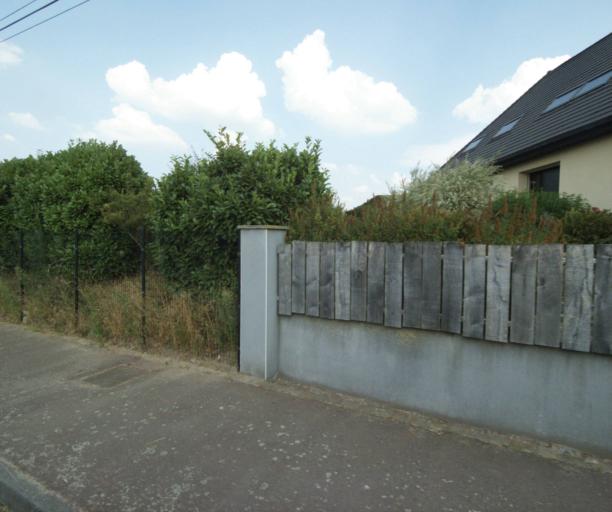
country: FR
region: Nord-Pas-de-Calais
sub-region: Departement du Nord
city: Linselles
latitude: 50.7275
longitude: 3.0596
